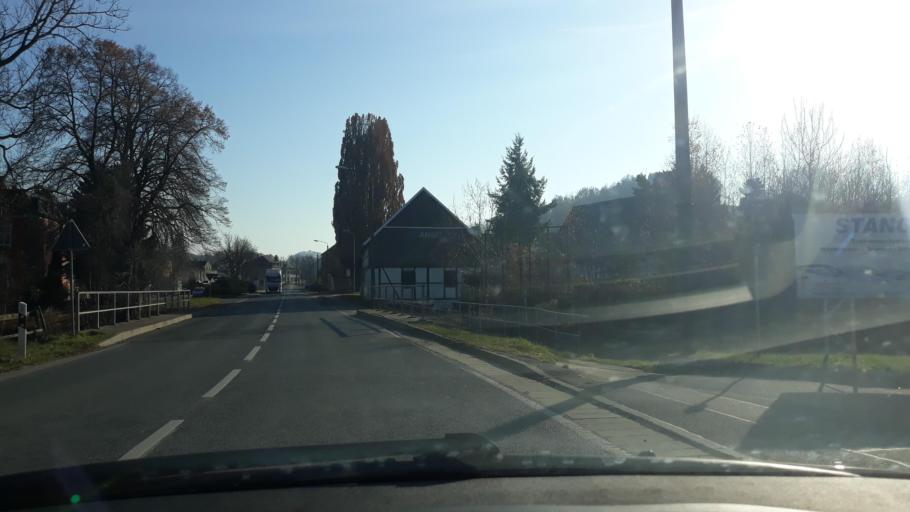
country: DE
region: Saxony
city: Kirchberg
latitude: 50.6461
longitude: 12.5152
